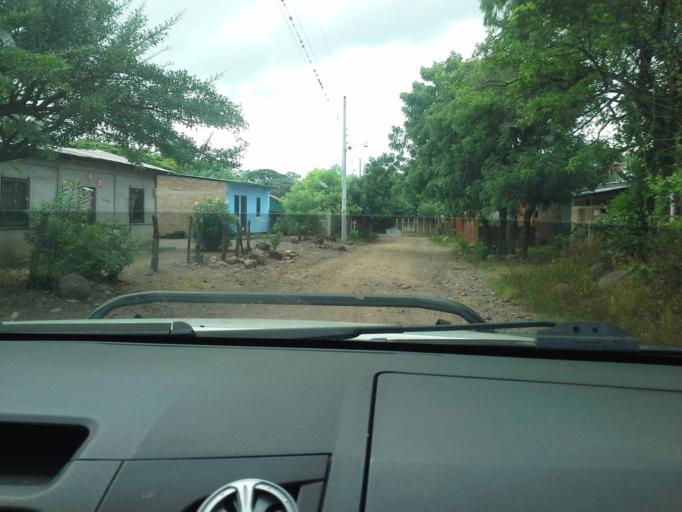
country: NI
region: Matagalpa
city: Ciudad Dario
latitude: 12.8352
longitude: -86.2150
